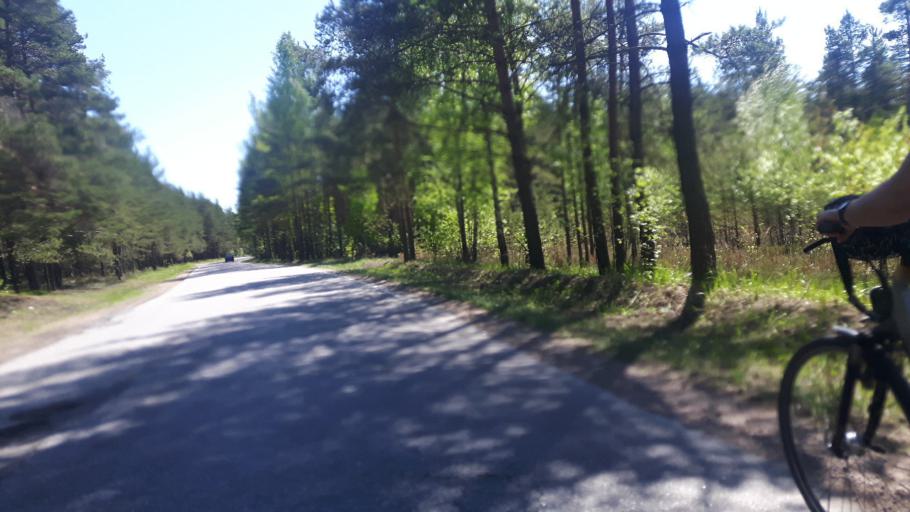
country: RU
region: Leningrad
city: Glebychevo
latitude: 60.3478
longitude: 28.8191
